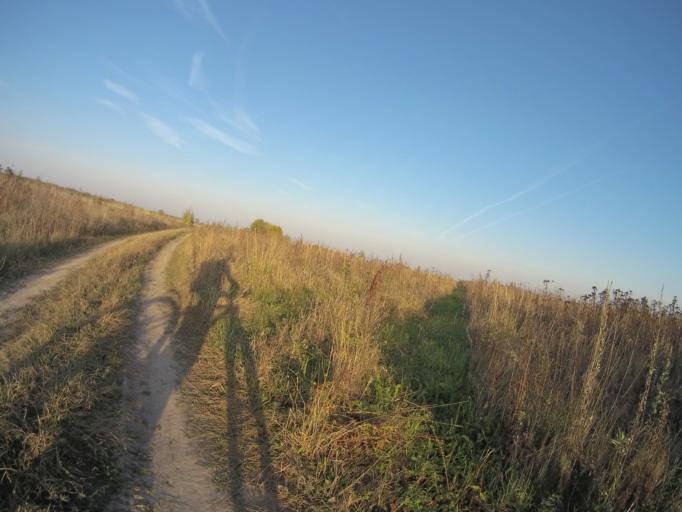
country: RU
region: Vladimir
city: Vladimir
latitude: 56.1673
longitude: 40.2840
